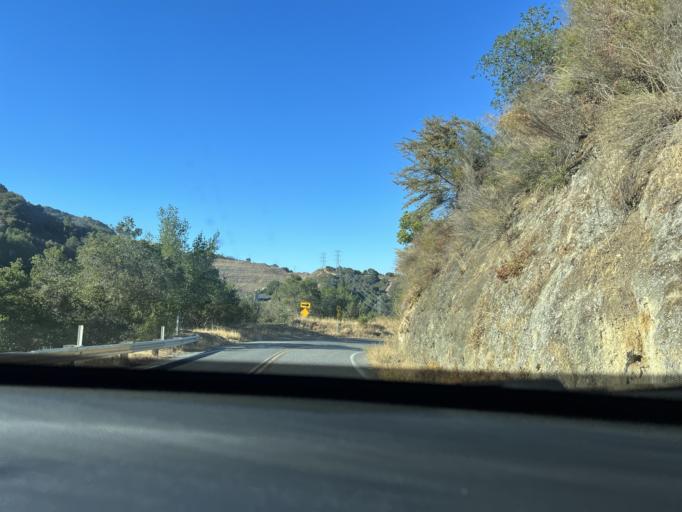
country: US
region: California
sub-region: Santa Clara County
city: Loyola
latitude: 37.2957
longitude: -122.0893
